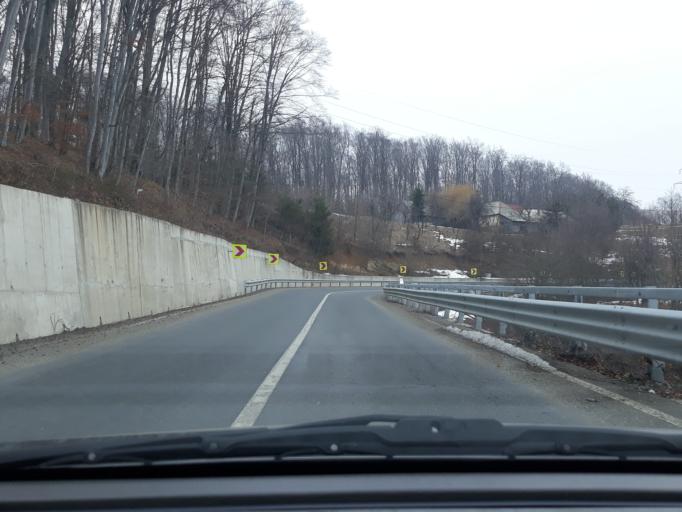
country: RO
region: Bihor
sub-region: Comuna Sinteu
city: Sinteu
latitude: 47.1213
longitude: 22.4600
